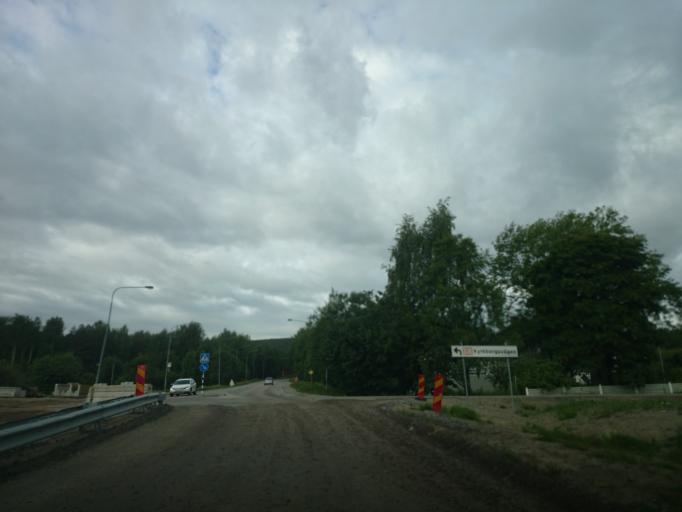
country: SE
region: Vaesternorrland
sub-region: Sundsvalls Kommun
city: Stockvik
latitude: 62.3752
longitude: 17.3616
